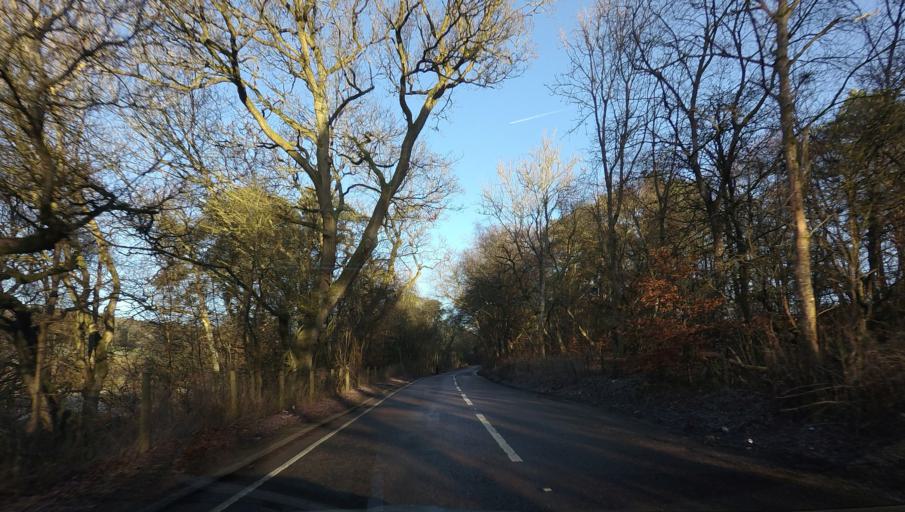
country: GB
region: Scotland
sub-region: North Lanarkshire
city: Newmains
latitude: 55.7984
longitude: -3.8502
